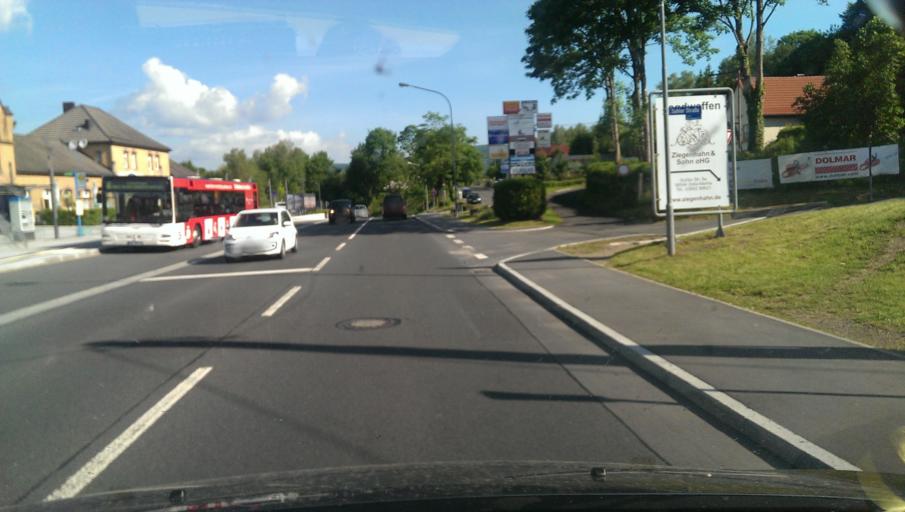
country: DE
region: Thuringia
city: Zella-Mehlis
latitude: 50.6461
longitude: 10.6752
